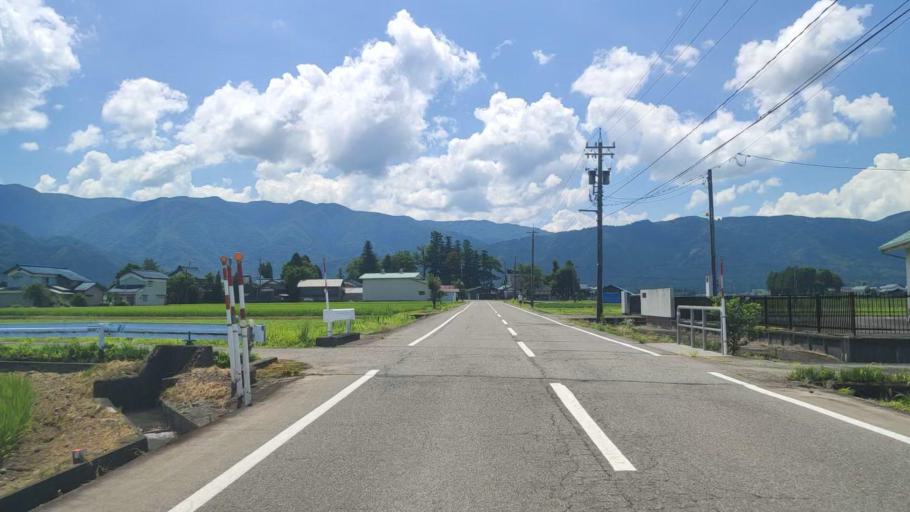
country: JP
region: Fukui
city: Ono
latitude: 35.9632
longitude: 136.5303
